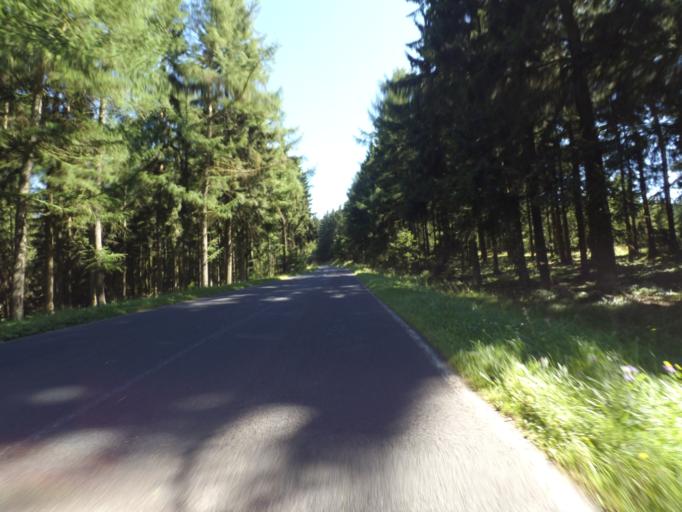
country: DE
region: Rheinland-Pfalz
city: Berndorf
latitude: 50.3325
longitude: 6.7058
